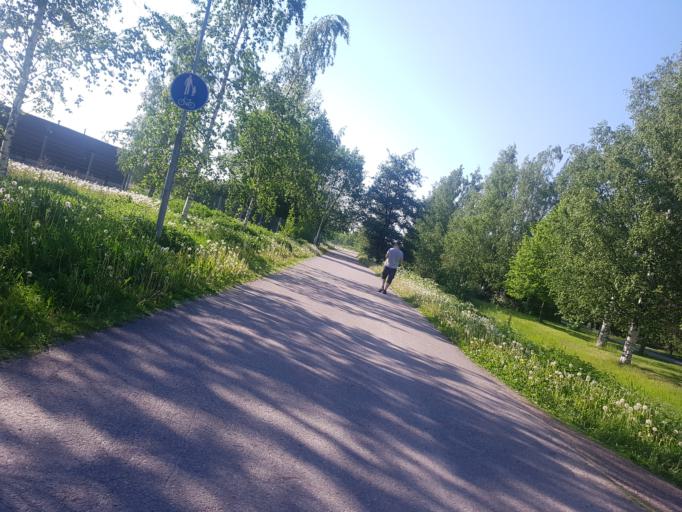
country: FI
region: Uusimaa
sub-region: Helsinki
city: Vantaa
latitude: 60.2488
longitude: 24.9976
